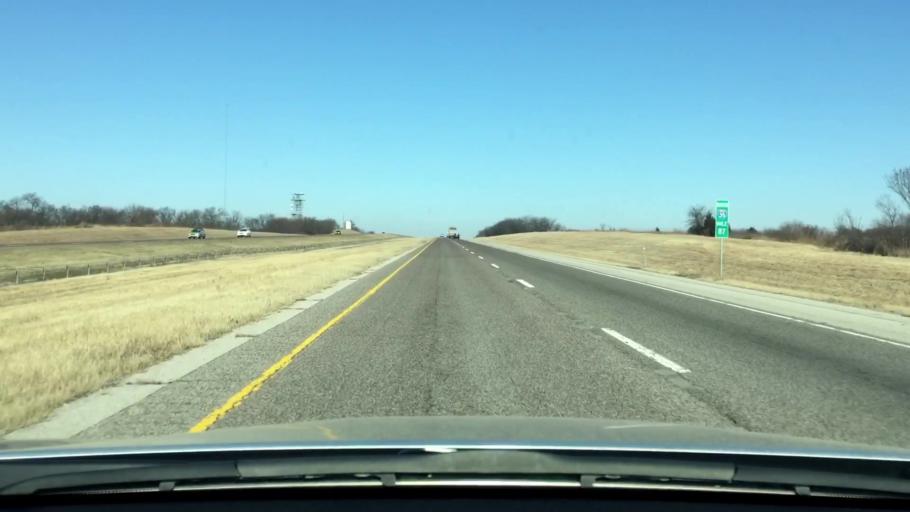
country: US
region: Oklahoma
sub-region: McClain County
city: Purcell
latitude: 34.9294
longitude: -97.3612
